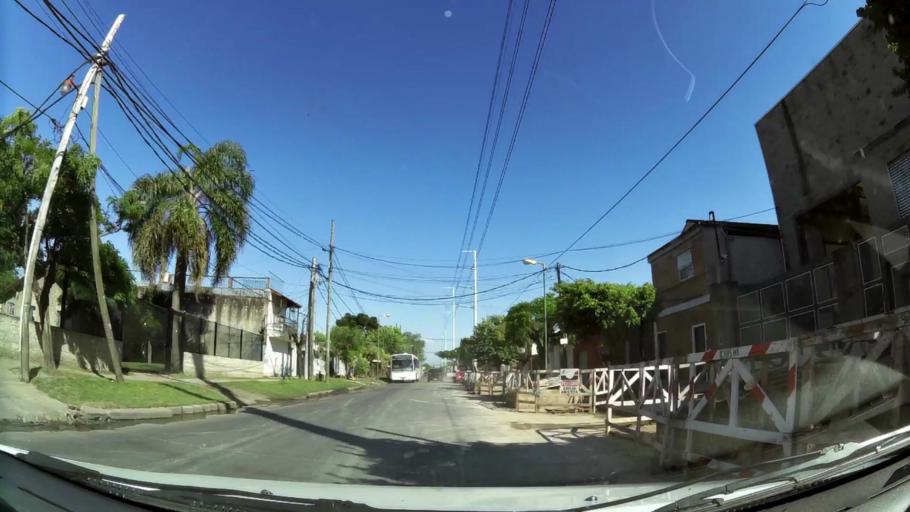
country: AR
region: Buenos Aires
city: Caseros
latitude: -34.5574
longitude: -58.5889
